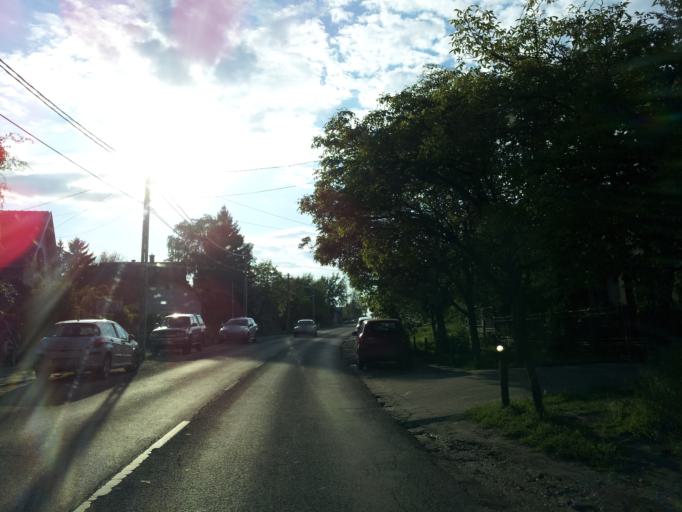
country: HU
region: Pest
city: Solymar
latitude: 47.5952
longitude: 18.9343
